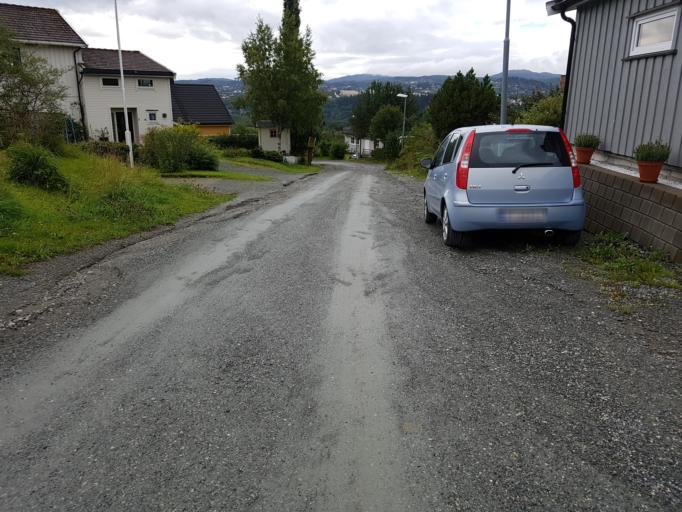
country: NO
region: Sor-Trondelag
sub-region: Trondheim
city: Trondheim
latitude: 63.3931
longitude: 10.4196
